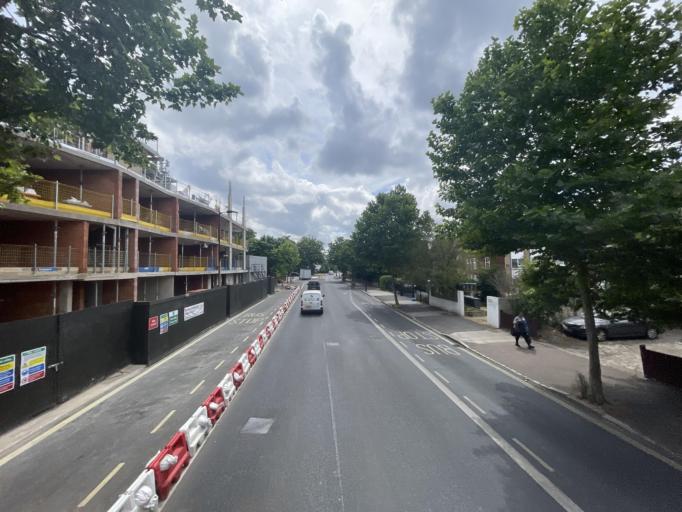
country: GB
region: England
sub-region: Greater London
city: Camberwell
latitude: 51.4619
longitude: -0.0915
